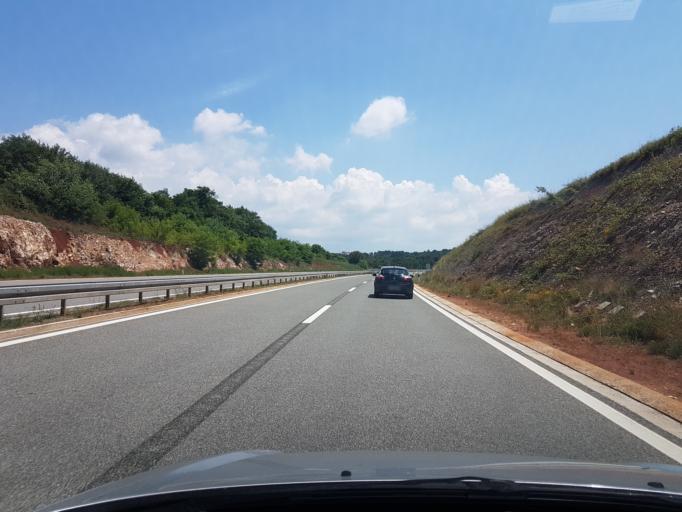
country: HR
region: Istarska
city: Buje
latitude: 45.3083
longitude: 13.7066
